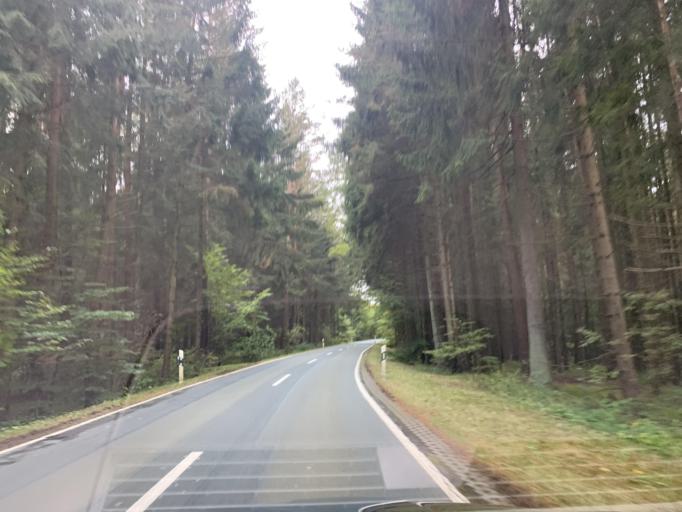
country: DE
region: Bavaria
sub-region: Upper Franconia
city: Pottenstein
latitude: 49.7305
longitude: 11.4441
